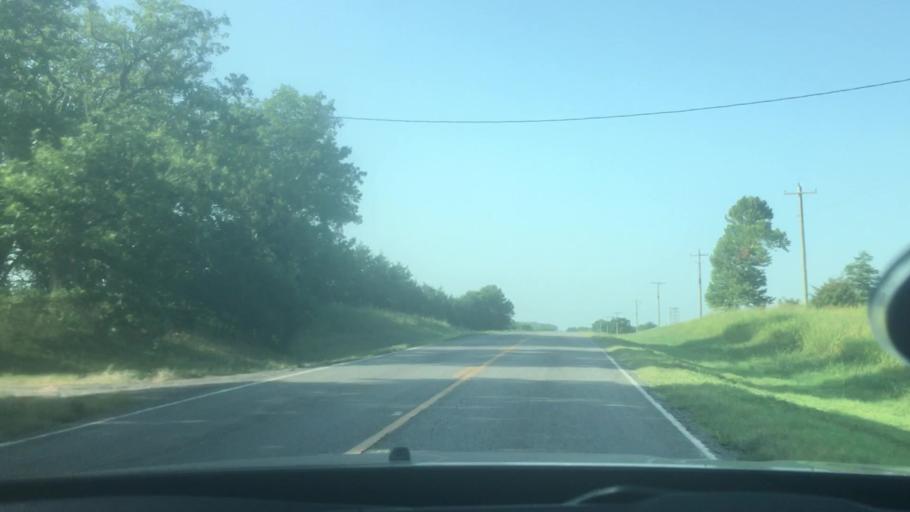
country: US
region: Oklahoma
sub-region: Coal County
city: Coalgate
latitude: 34.3917
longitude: -96.4246
